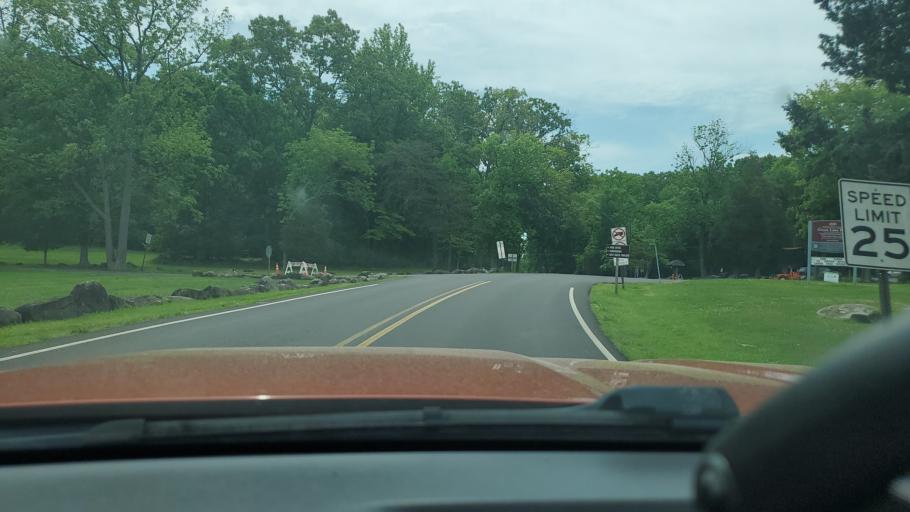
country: US
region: Pennsylvania
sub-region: Montgomery County
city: Red Hill
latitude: 40.3309
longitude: -75.4865
